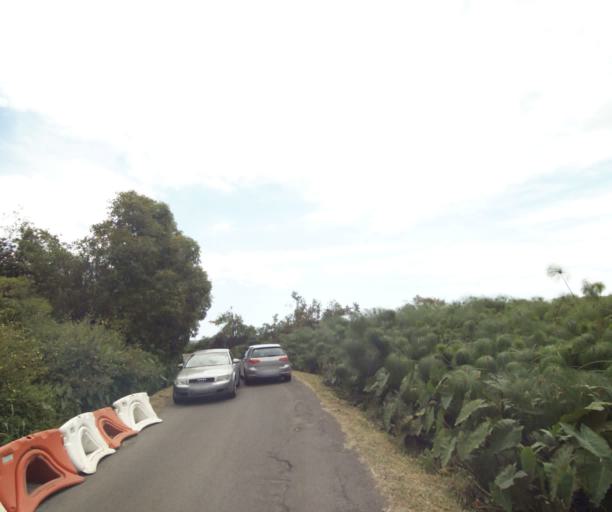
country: RE
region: Reunion
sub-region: Reunion
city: Saint-Paul
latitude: -20.9988
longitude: 55.3031
